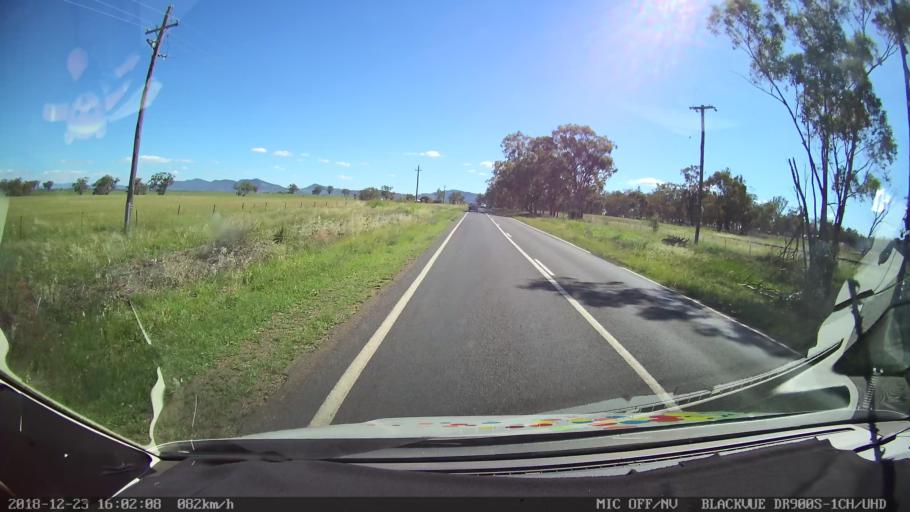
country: AU
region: New South Wales
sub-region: Tamworth Municipality
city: Phillip
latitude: -31.2289
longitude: 150.8115
